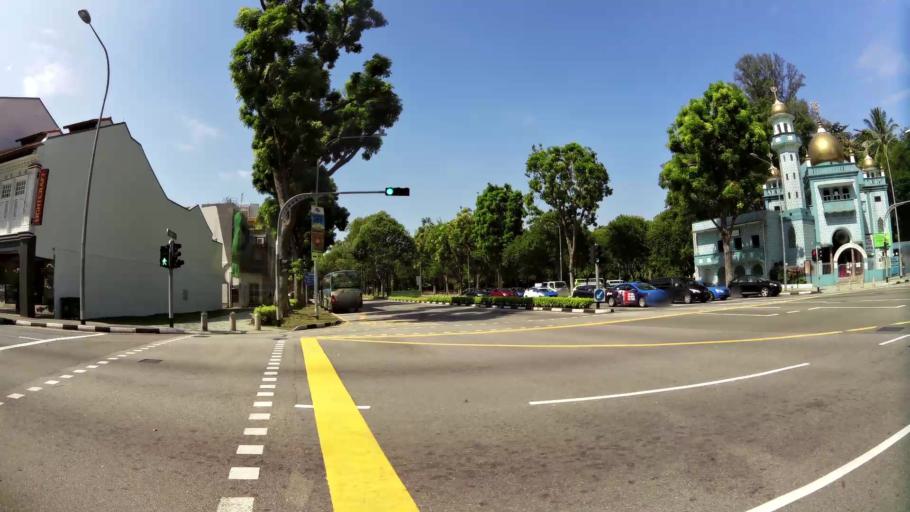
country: SG
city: Singapore
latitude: 1.3050
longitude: 103.8602
